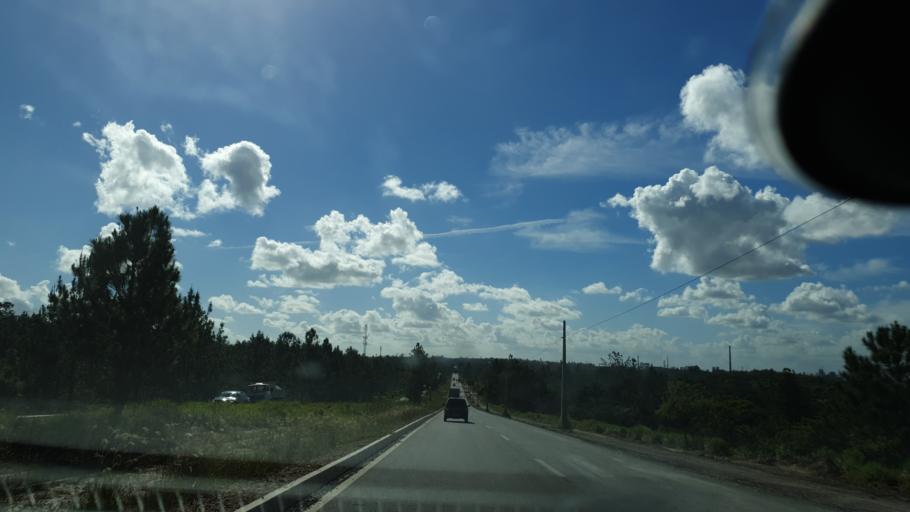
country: BR
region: Bahia
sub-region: Camacari
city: Camacari
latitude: -12.6824
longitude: -38.2916
